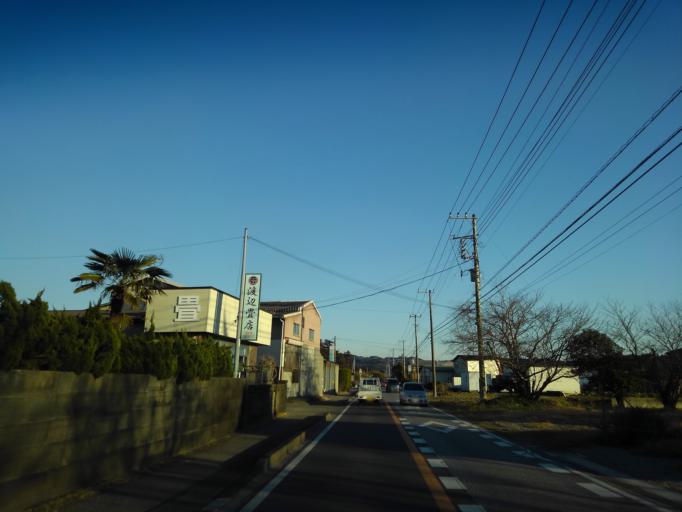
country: JP
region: Chiba
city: Kimitsu
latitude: 35.3033
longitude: 139.9704
